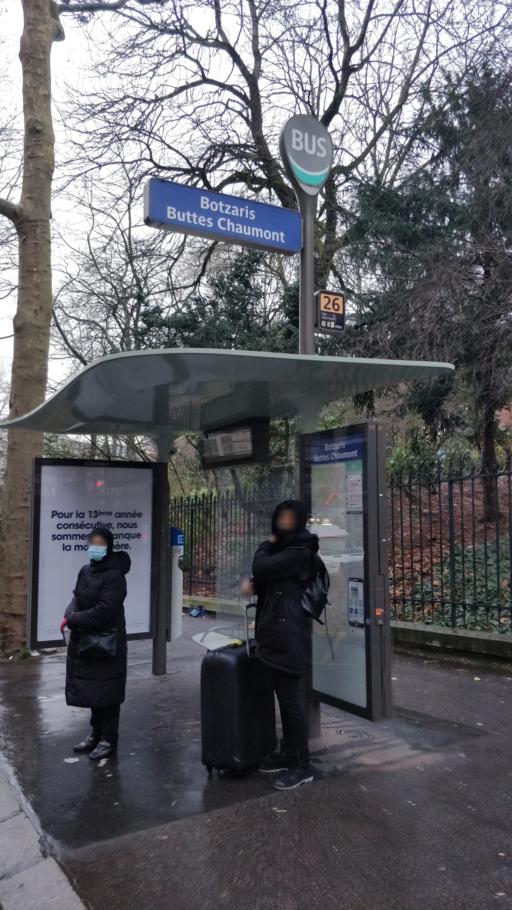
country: FR
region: Ile-de-France
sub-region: Departement de Seine-Saint-Denis
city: Le Pre-Saint-Gervais
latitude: 48.8761
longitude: 2.3808
